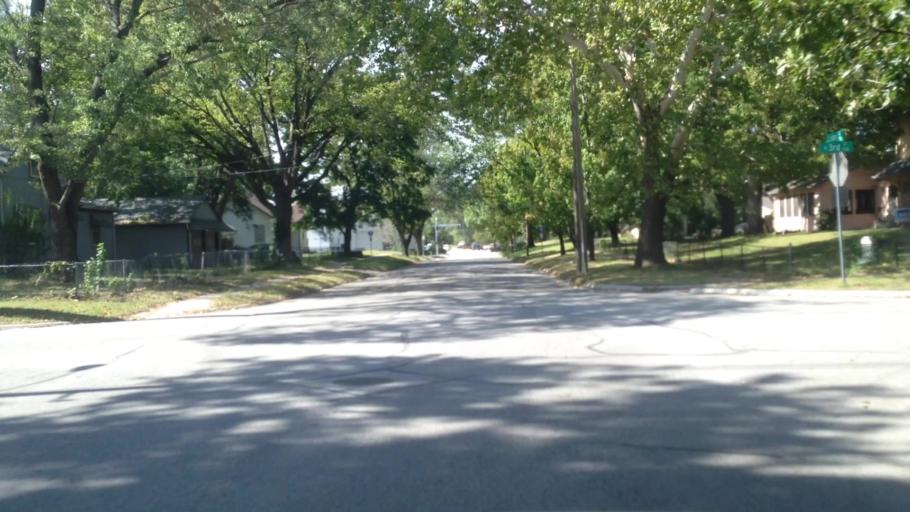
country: US
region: Kansas
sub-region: Douglas County
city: Lawrence
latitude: 38.9825
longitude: -95.2330
